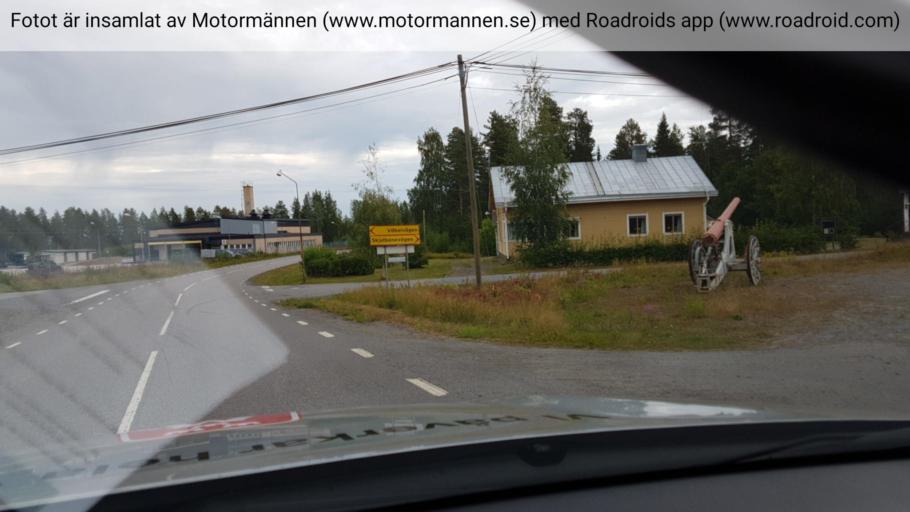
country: SE
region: Norrbotten
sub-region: Bodens Kommun
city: Boden
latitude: 65.7973
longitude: 21.6542
